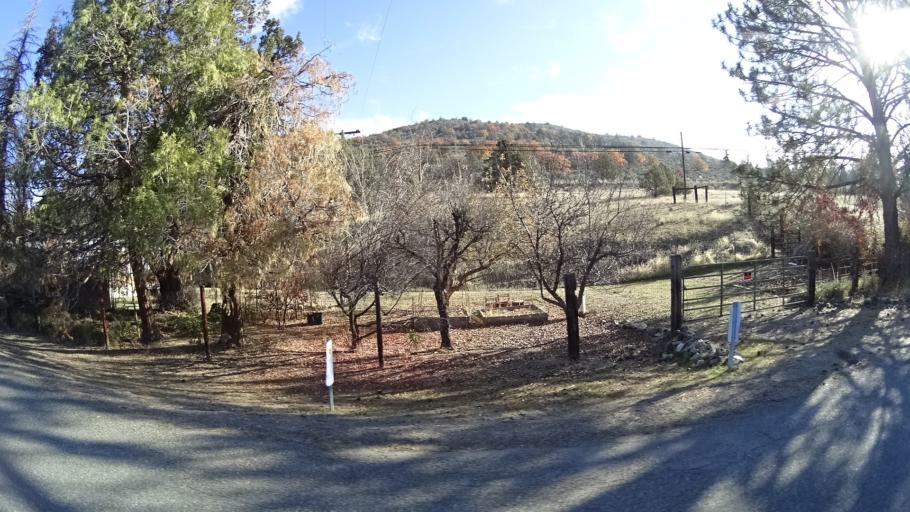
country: US
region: California
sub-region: Siskiyou County
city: Yreka
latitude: 41.6845
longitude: -122.6316
